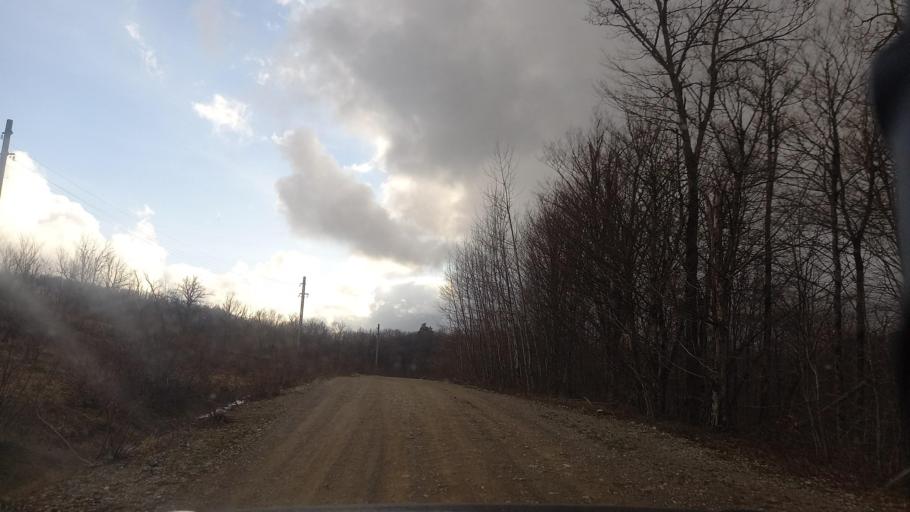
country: RU
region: Krasnodarskiy
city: Dzhubga
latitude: 44.5222
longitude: 38.7709
